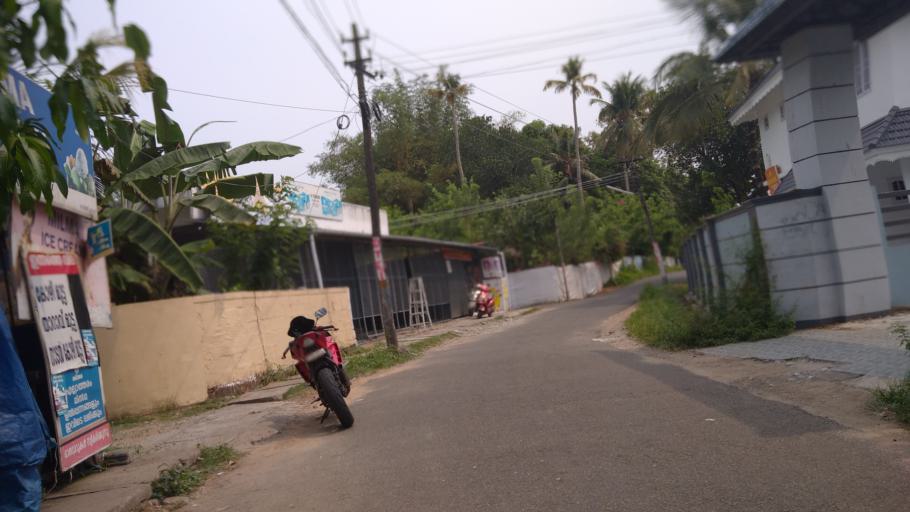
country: IN
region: Kerala
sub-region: Ernakulam
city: Elur
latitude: 10.1487
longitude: 76.2548
